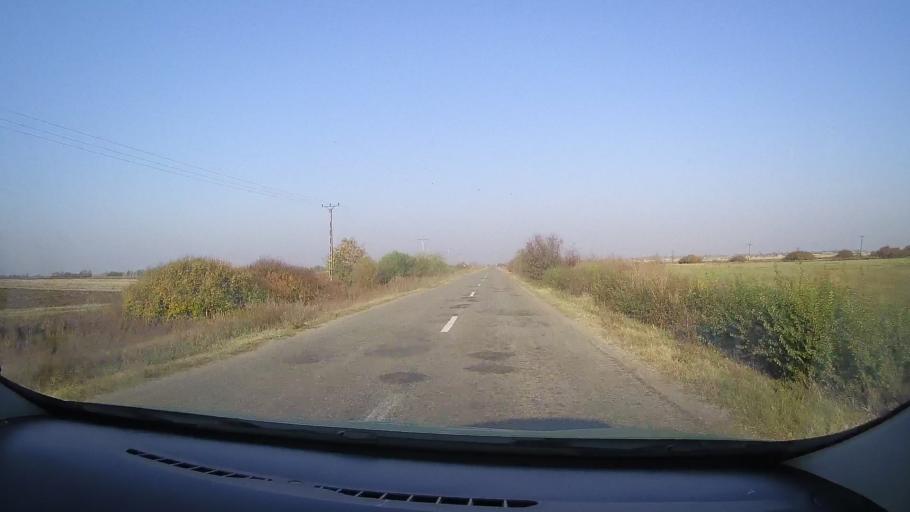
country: RO
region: Arad
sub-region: Comuna Graniceri
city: Graniceri
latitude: 46.5075
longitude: 21.3216
